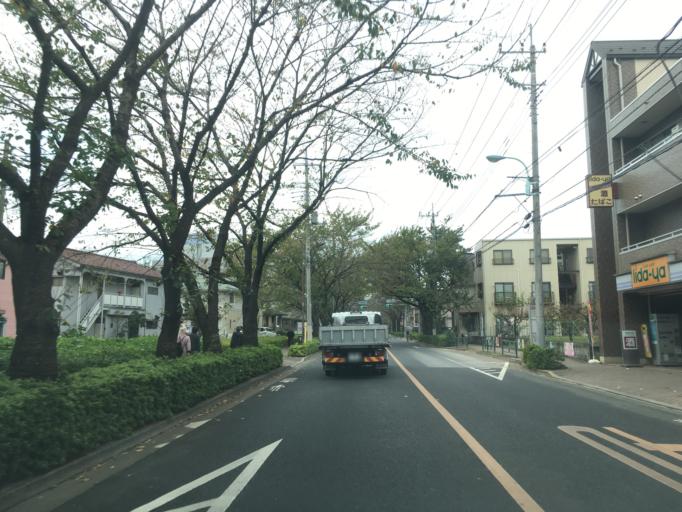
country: JP
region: Tokyo
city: Chofugaoka
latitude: 35.6334
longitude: 139.5693
